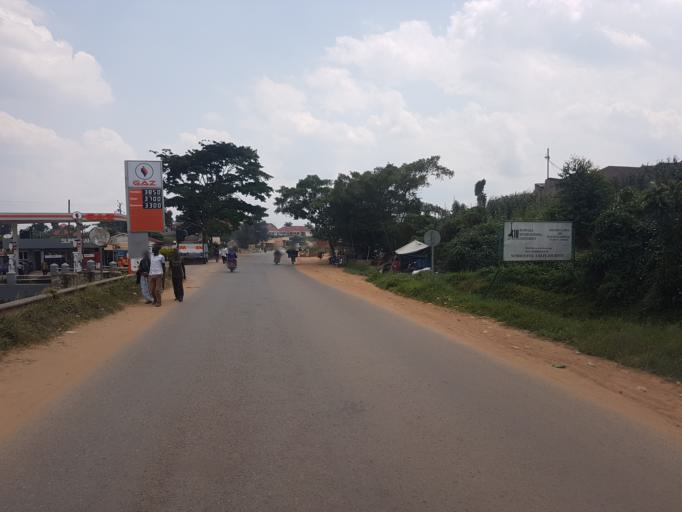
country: UG
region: Western Region
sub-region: Bushenyi District
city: Bushenyi
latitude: -0.5450
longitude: 30.1374
